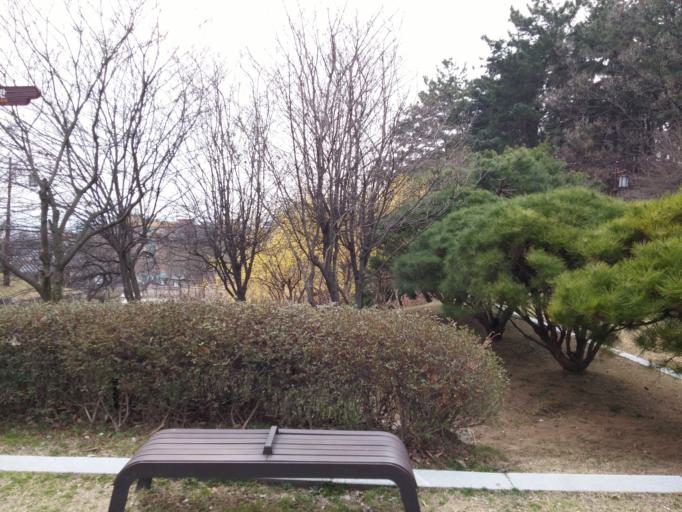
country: KR
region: Daejeon
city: Daejeon
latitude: 36.3477
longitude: 127.4582
